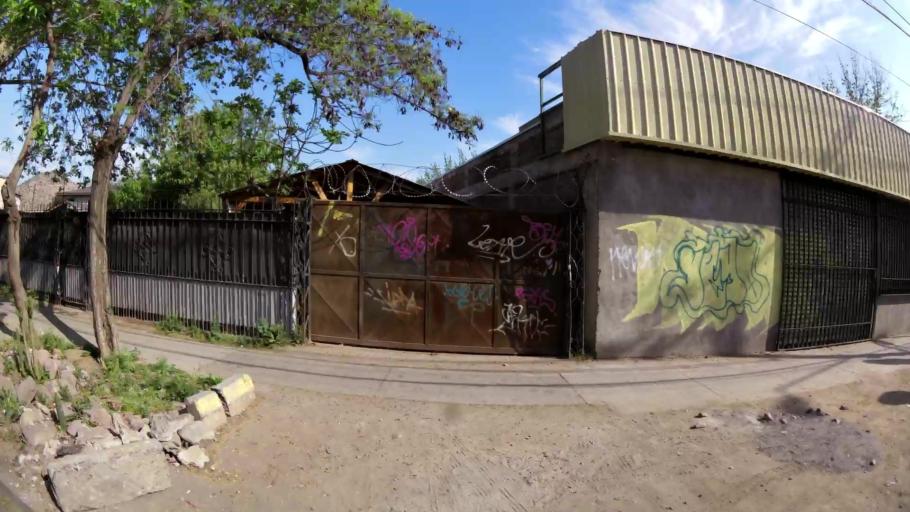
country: CL
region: Santiago Metropolitan
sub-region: Provincia de Maipo
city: San Bernardo
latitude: -33.5985
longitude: -70.7092
